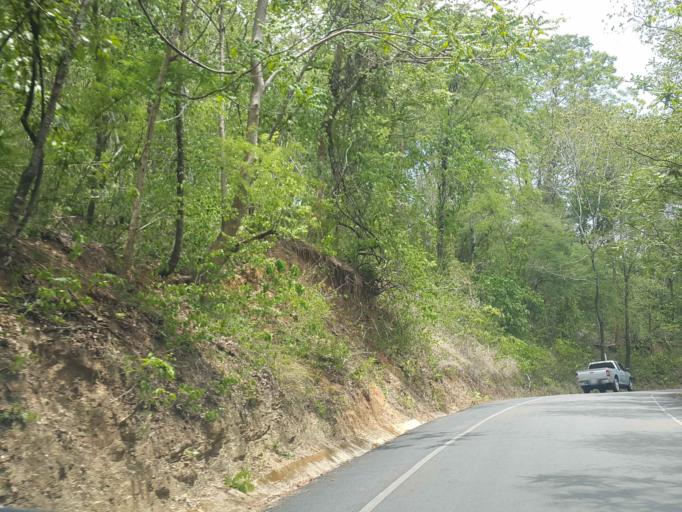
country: TH
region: Chiang Mai
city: Hang Dong
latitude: 18.7560
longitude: 98.9169
